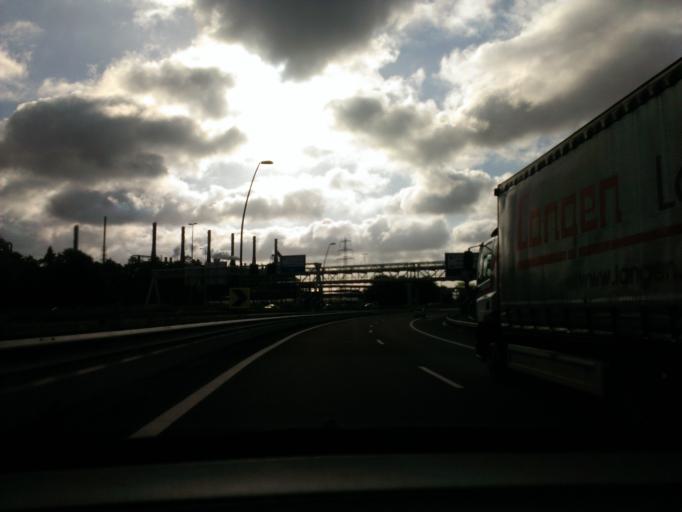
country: NL
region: Limburg
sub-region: Gemeente Stein
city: Stein
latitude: 50.9655
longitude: 5.7910
